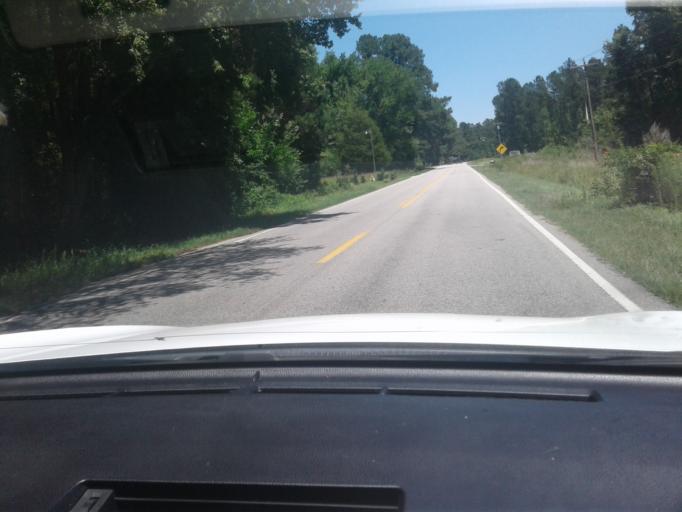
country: US
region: North Carolina
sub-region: Harnett County
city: Erwin
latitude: 35.3176
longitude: -78.7121
